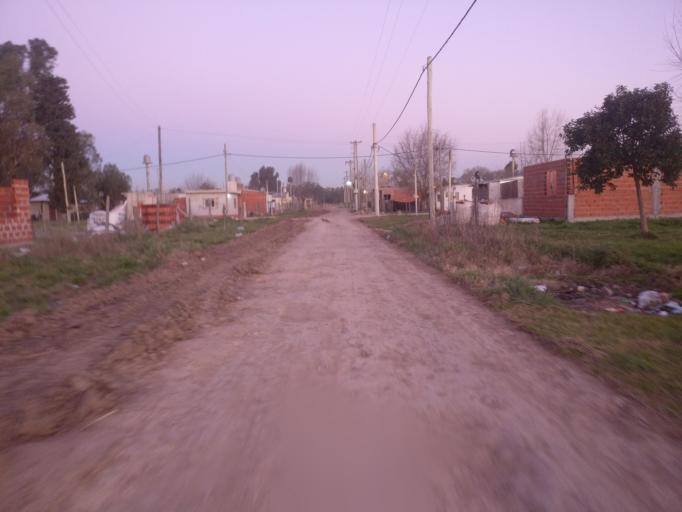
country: AR
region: Buenos Aires
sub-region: Partido de Ezeiza
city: Ezeiza
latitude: -34.9392
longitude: -58.6041
